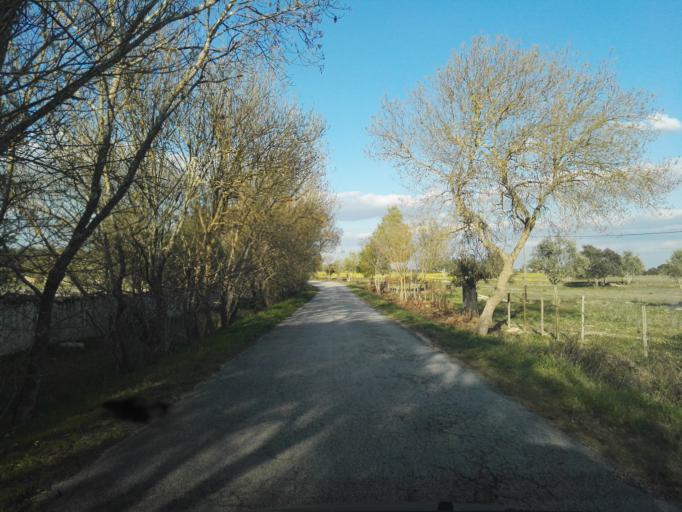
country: PT
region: Evora
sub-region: Evora
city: Evora
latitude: 38.5377
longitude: -7.9406
